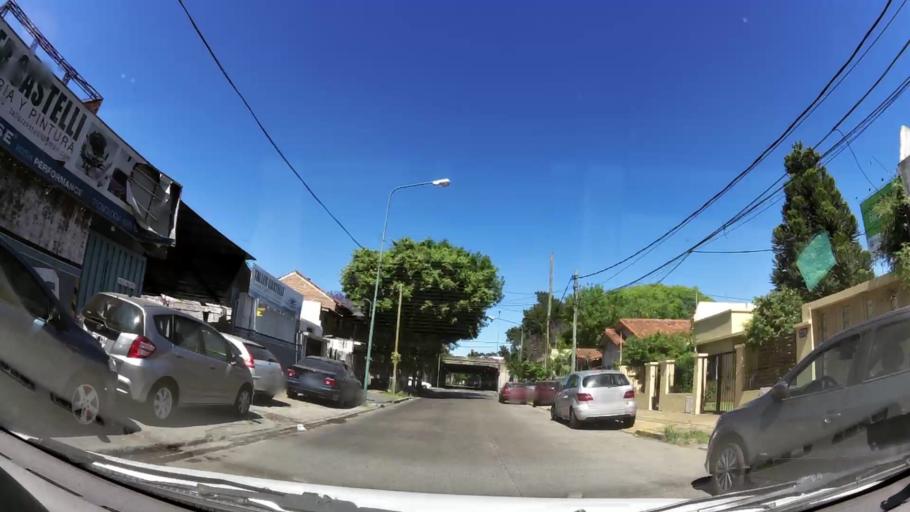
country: AR
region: Buenos Aires
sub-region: Partido de Vicente Lopez
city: Olivos
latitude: -34.5257
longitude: -58.5079
